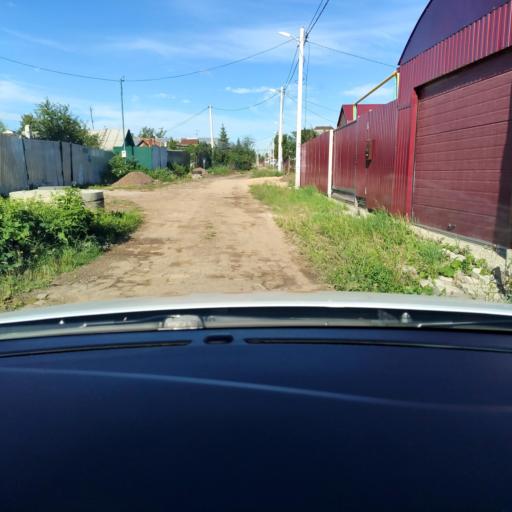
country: RU
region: Tatarstan
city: Verkhniy Uslon
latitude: 55.8018
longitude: 49.0367
